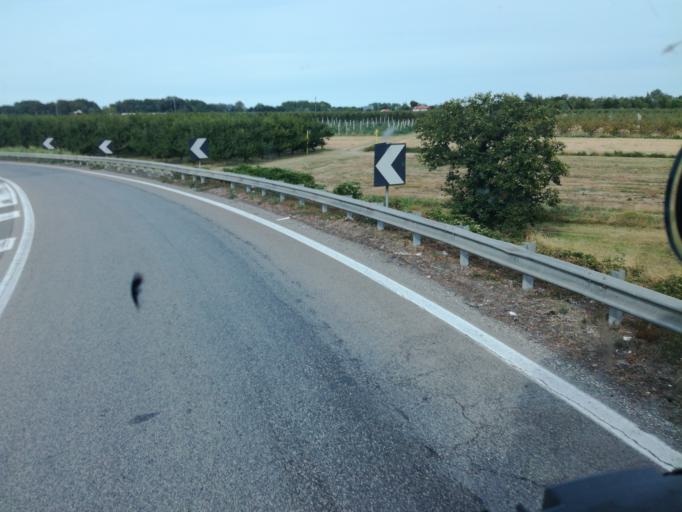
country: IT
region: Emilia-Romagna
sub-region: Forli-Cesena
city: Santa Maria Nuova
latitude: 44.1899
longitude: 12.2255
